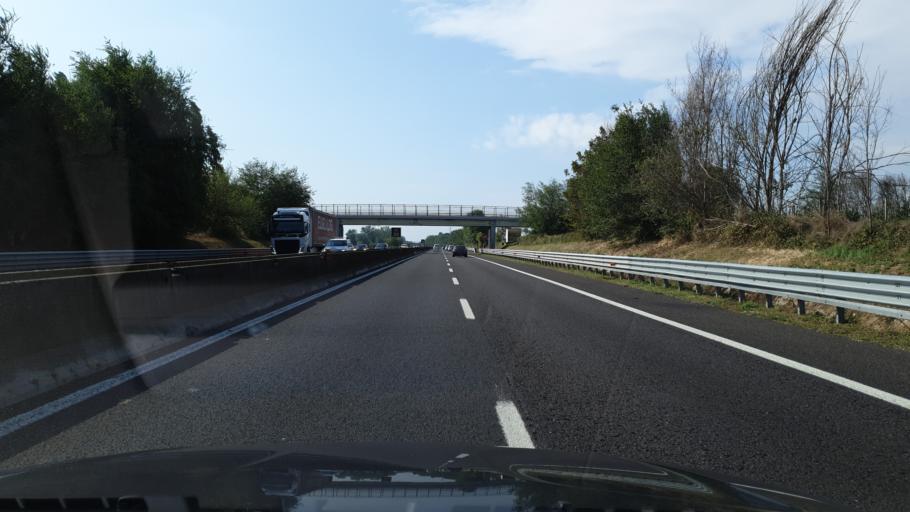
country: IT
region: Emilia-Romagna
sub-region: Provincia di Ferrara
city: Porotto-Cassama
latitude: 44.8217
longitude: 11.5570
